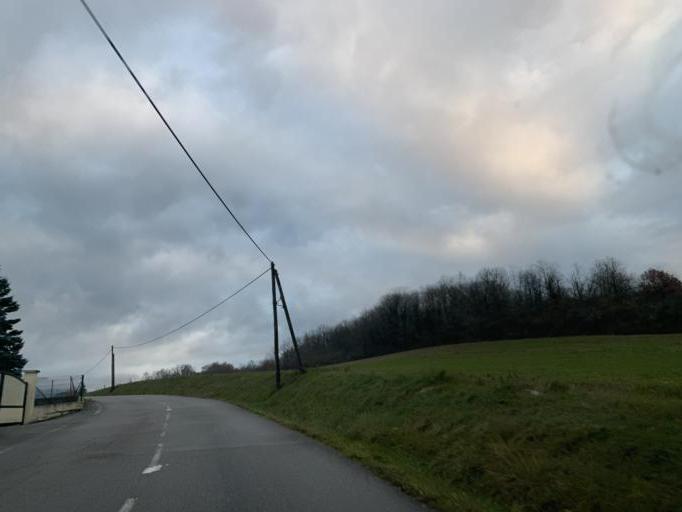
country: FR
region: Rhone-Alpes
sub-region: Departement de l'Ain
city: Belley
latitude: 45.7906
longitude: 5.6924
